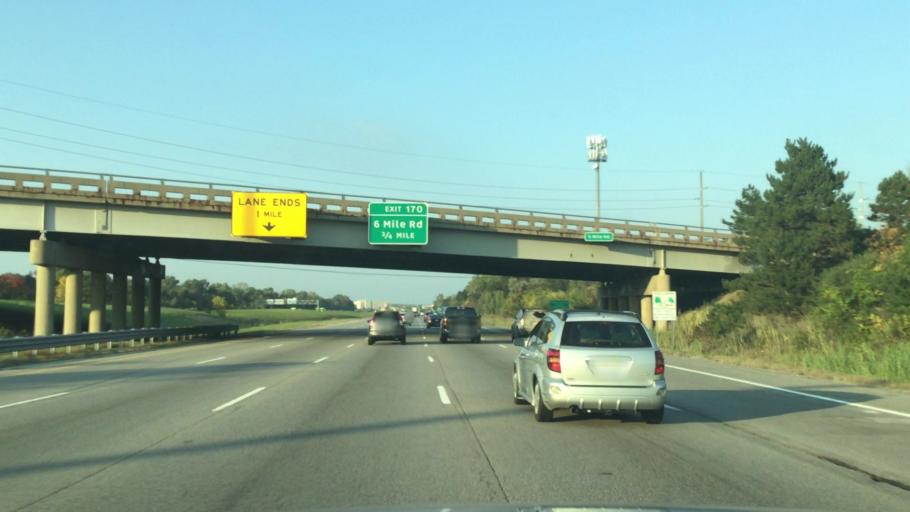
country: US
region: Michigan
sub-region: Wayne County
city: Plymouth
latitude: 42.3954
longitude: -83.4312
